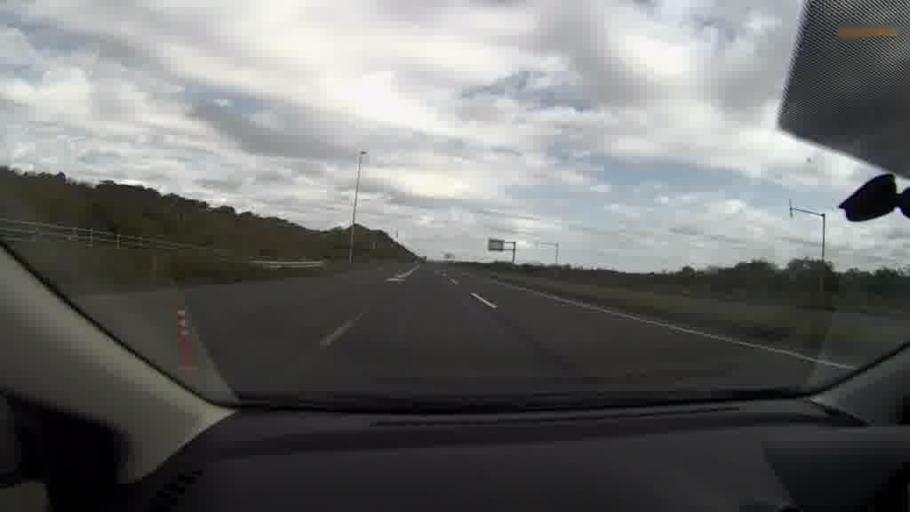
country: JP
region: Hokkaido
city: Kushiro
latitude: 43.0120
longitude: 144.2566
